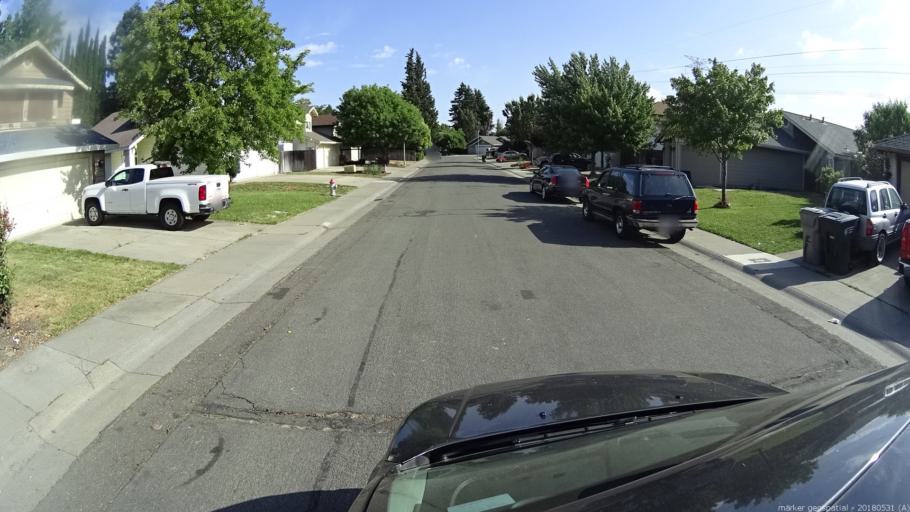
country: US
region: California
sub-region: Sacramento County
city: Sacramento
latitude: 38.6307
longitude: -121.4852
